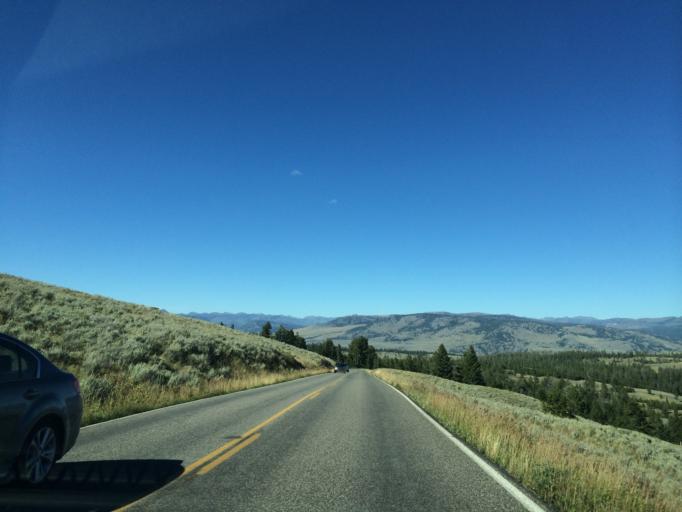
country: US
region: Montana
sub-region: Gallatin County
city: West Yellowstone
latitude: 44.8599
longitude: -110.4091
